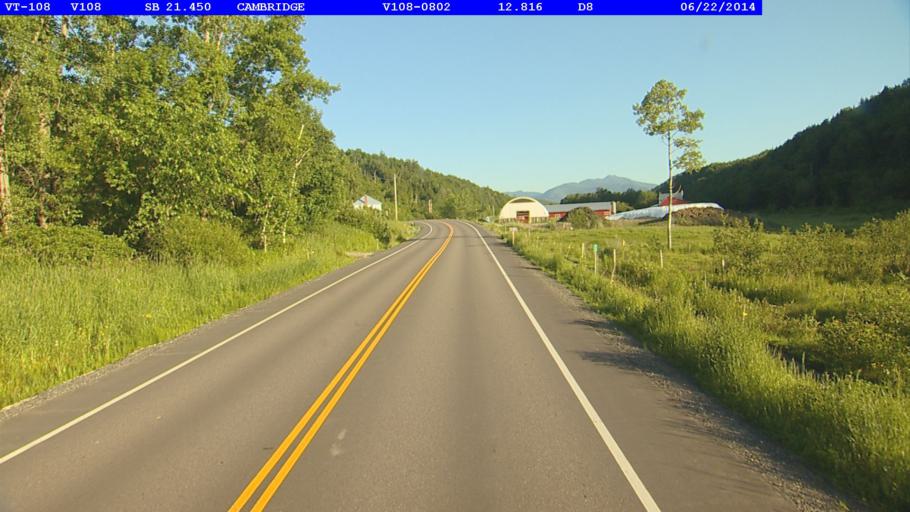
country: US
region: Vermont
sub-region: Lamoille County
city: Johnson
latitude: 44.6995
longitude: -72.8295
